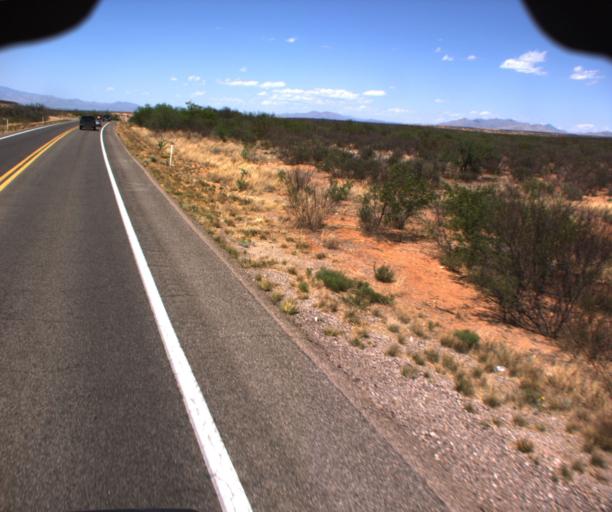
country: US
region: Arizona
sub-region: Cochise County
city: Saint David
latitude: 31.8065
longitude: -110.1619
